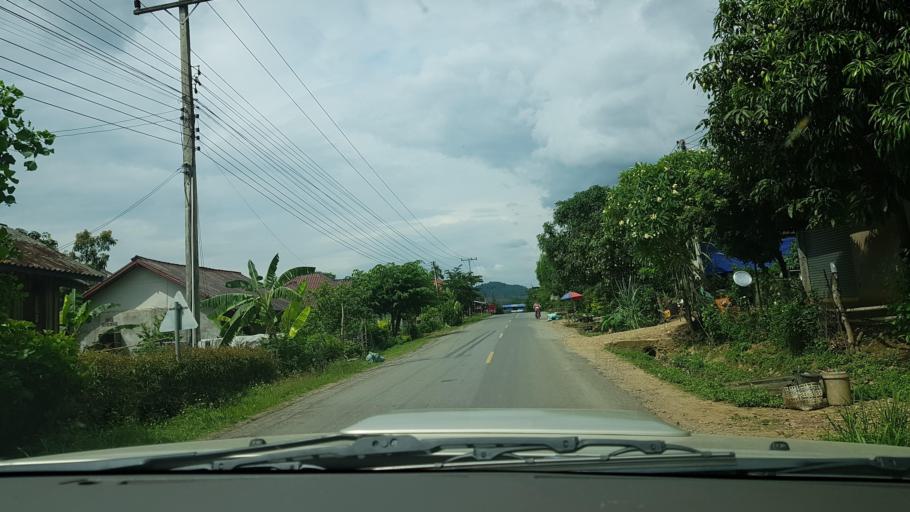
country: LA
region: Loungnamtha
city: Muang Nale
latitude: 20.3202
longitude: 101.6592
